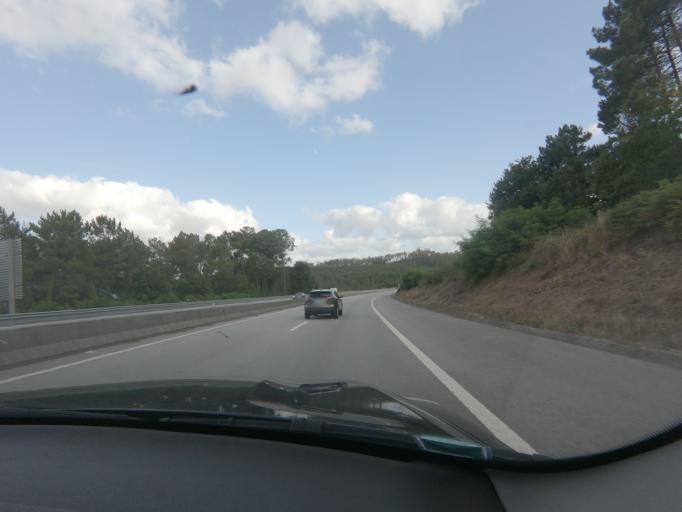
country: PT
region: Viseu
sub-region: Viseu
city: Abraveses
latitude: 40.6584
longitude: -7.9680
